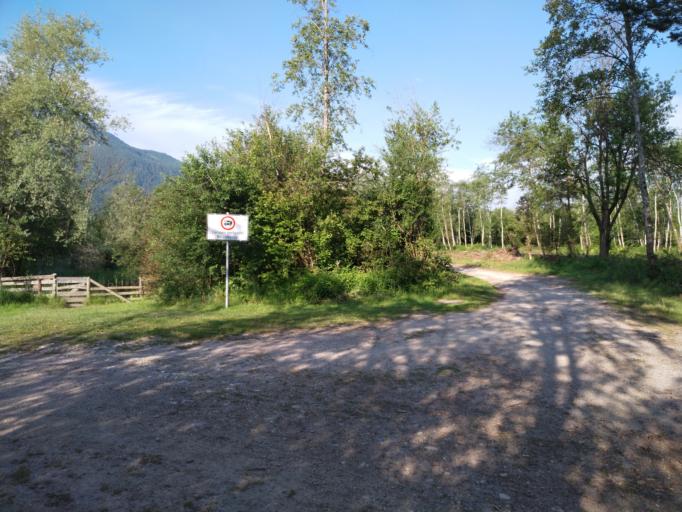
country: AT
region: Carinthia
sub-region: Politischer Bezirk Klagenfurt Land
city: Ebenthal
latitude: 46.5499
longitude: 14.3910
